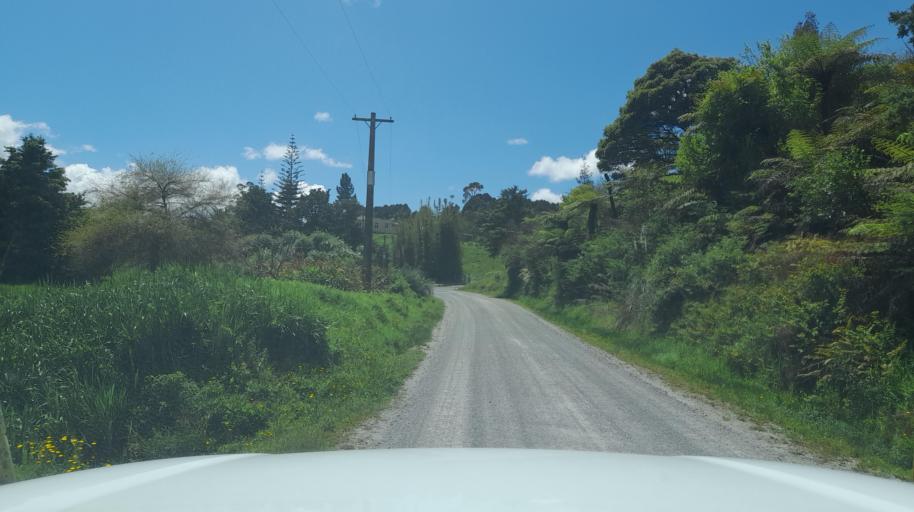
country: NZ
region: Northland
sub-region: Far North District
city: Taipa
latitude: -35.1236
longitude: 173.4081
